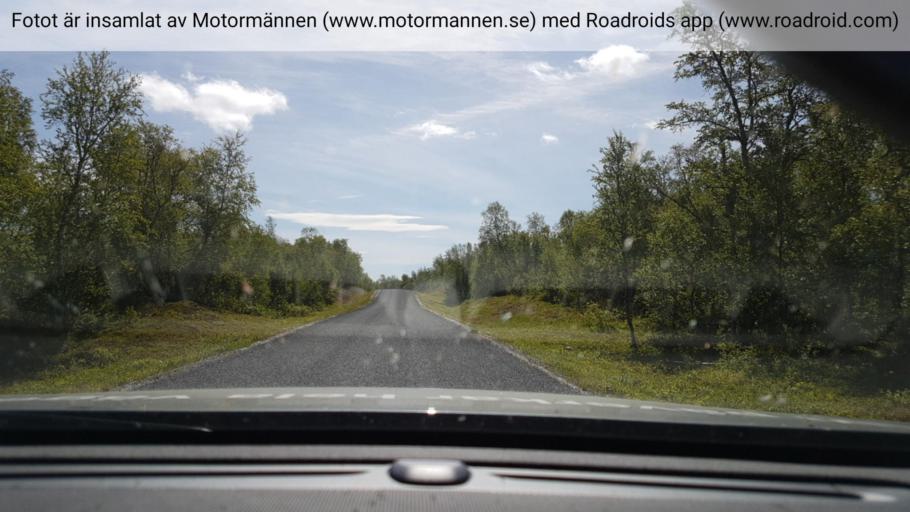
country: NO
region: Nordland
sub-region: Hattfjelldal
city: Hattfjelldal
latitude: 65.4050
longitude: 14.9493
